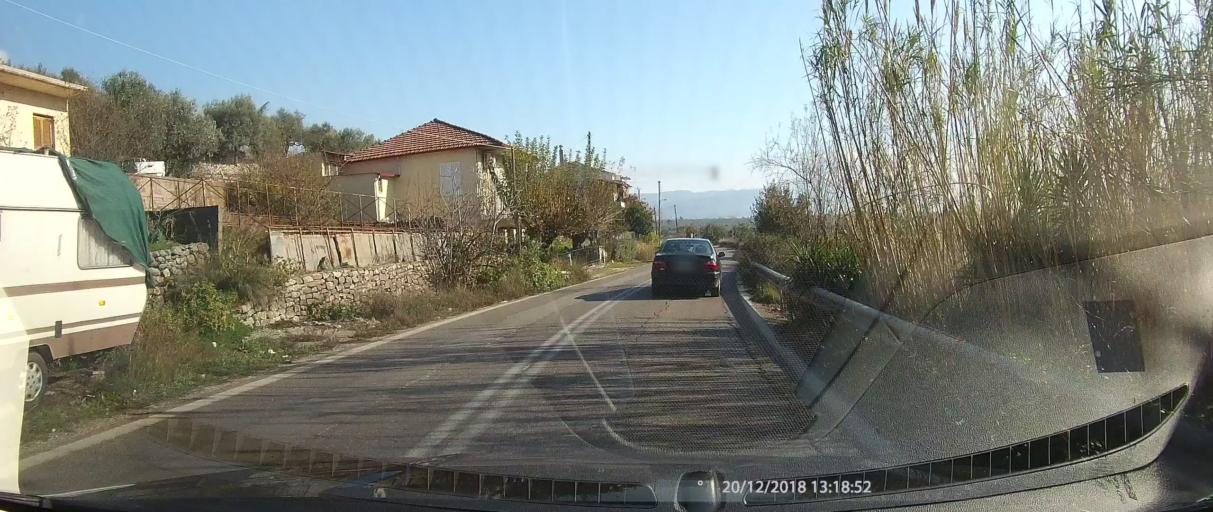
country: GR
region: West Greece
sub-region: Nomos Aitolias kai Akarnanias
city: Paravola
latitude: 38.6139
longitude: 21.5262
